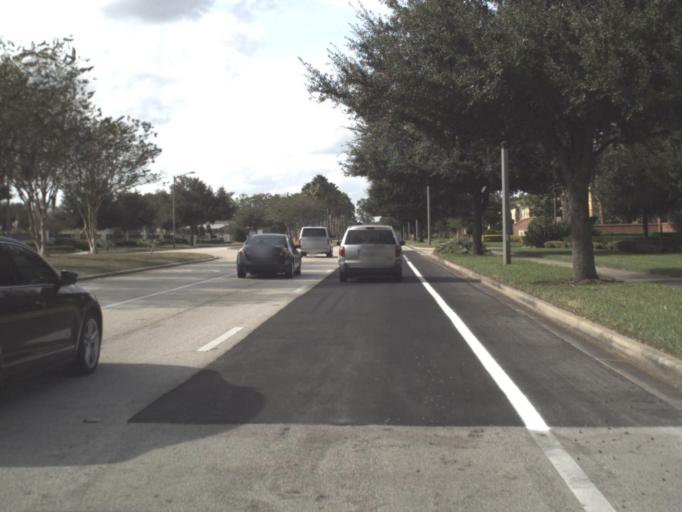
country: US
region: Florida
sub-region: Orange County
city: Conway
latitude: 28.4252
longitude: -81.2516
